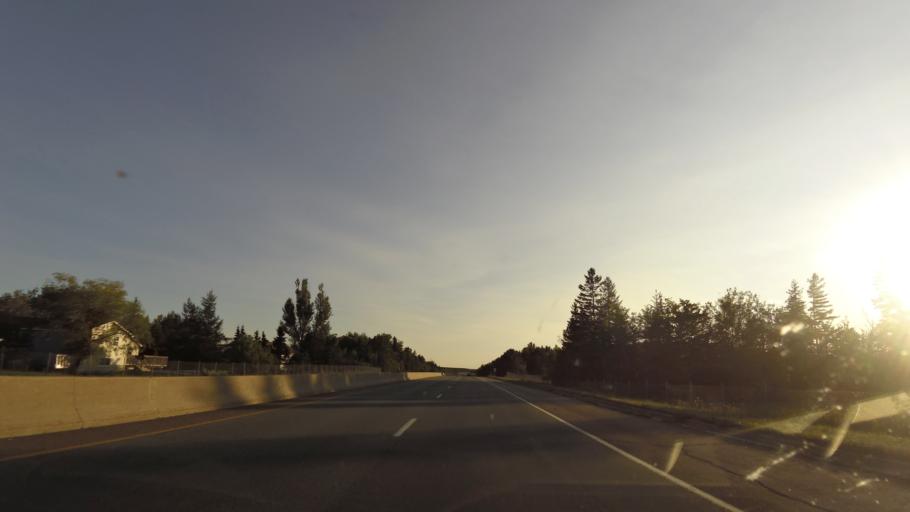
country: CA
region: New Brunswick
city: Salisbury
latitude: 45.9274
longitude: -65.1711
